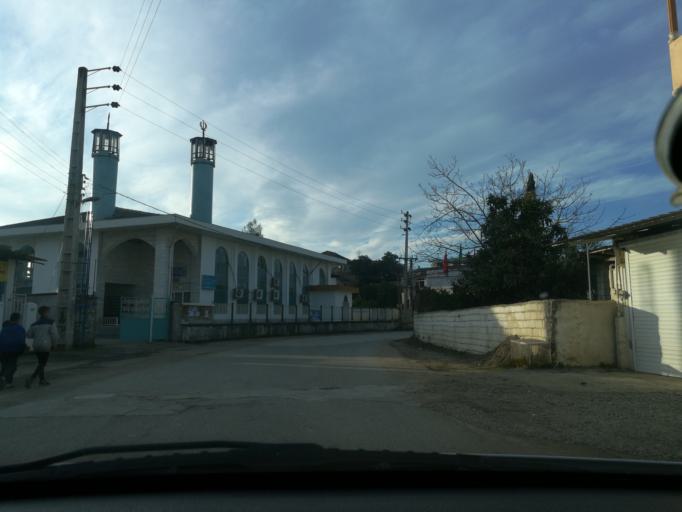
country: IR
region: Mazandaran
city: Chalus
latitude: 36.6421
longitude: 51.4390
